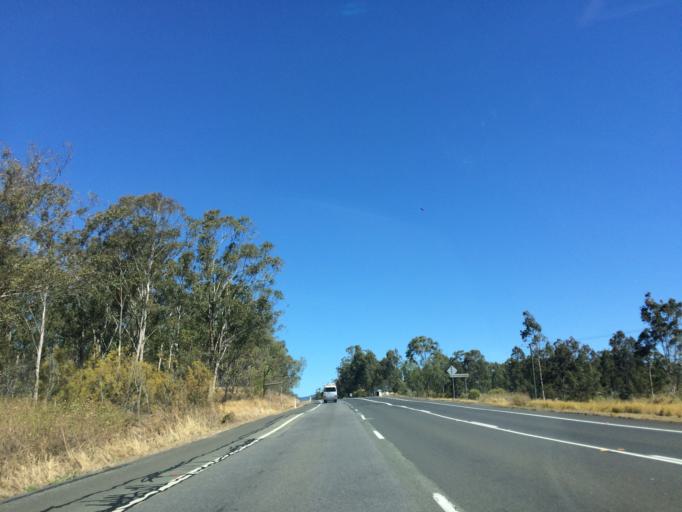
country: AU
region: Queensland
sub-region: Ipswich
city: Thagoona
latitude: -28.0123
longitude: 152.5224
